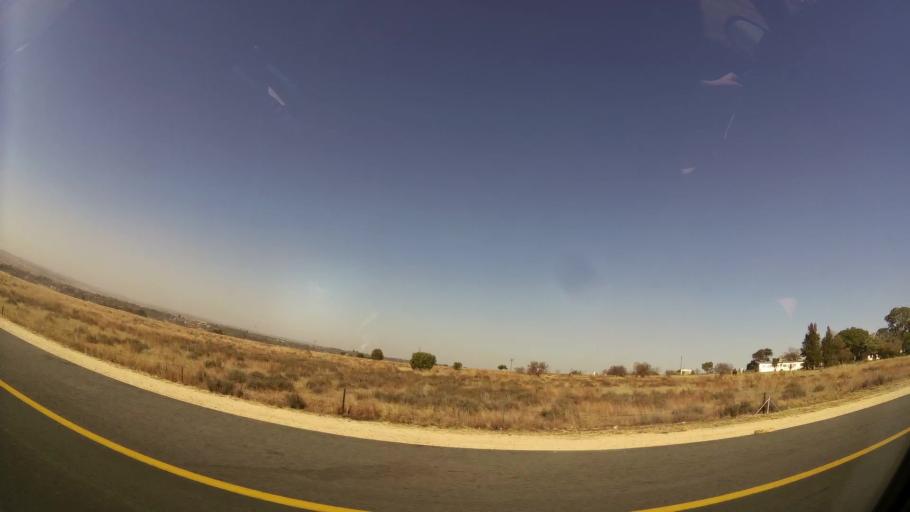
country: ZA
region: Gauteng
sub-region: City of Johannesburg Metropolitan Municipality
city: Diepsloot
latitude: -25.9676
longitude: 27.9471
